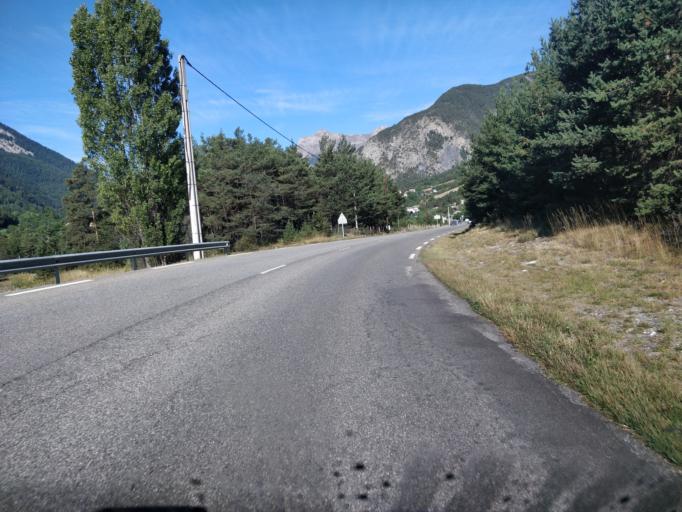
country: FR
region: Provence-Alpes-Cote d'Azur
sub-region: Departement des Alpes-de-Haute-Provence
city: Barcelonnette
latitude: 44.3901
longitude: 6.5813
